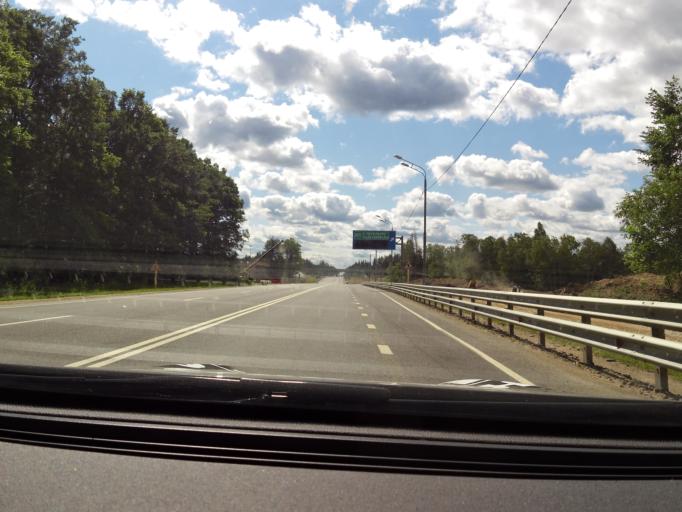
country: RU
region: Tverskaya
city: Vydropuzhsk
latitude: 57.2281
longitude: 34.9231
